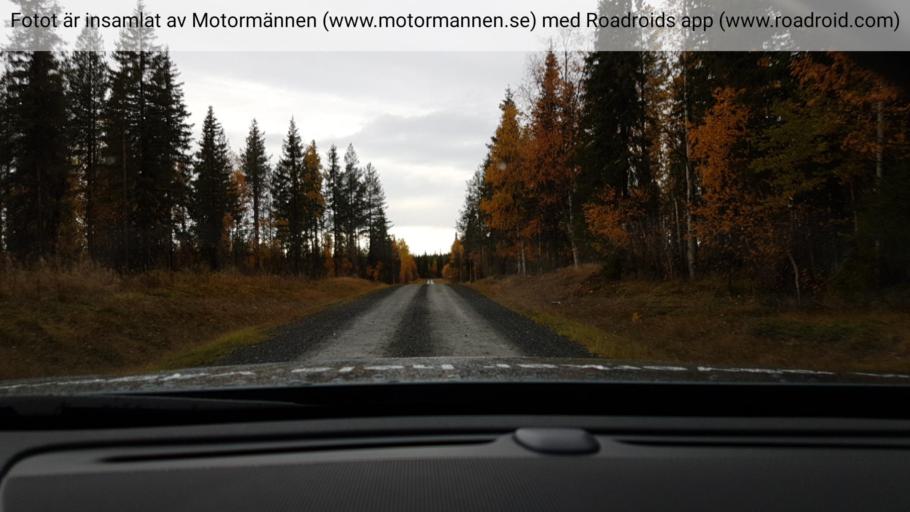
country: SE
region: Norrbotten
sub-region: Pajala Kommun
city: Pajala
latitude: 67.1005
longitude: 22.7154
